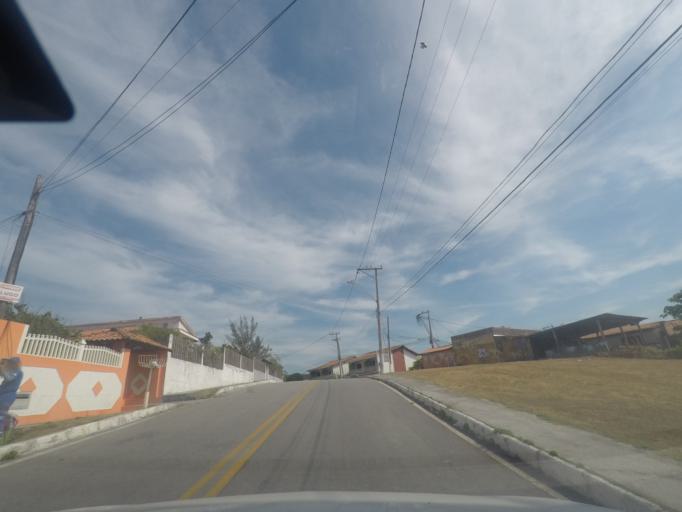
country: BR
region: Rio de Janeiro
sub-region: Marica
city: Marica
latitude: -22.9585
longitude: -42.8140
